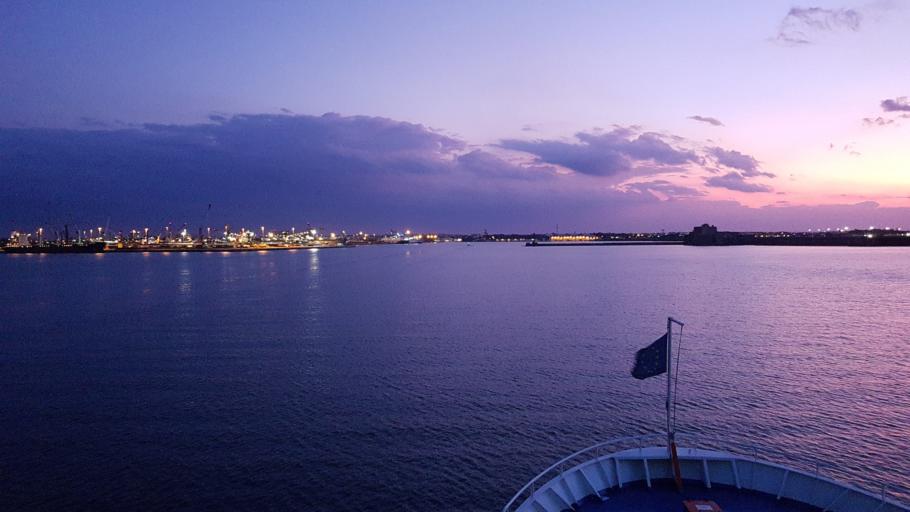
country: IT
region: Apulia
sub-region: Provincia di Brindisi
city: Materdomini
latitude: 40.6572
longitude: 17.9814
